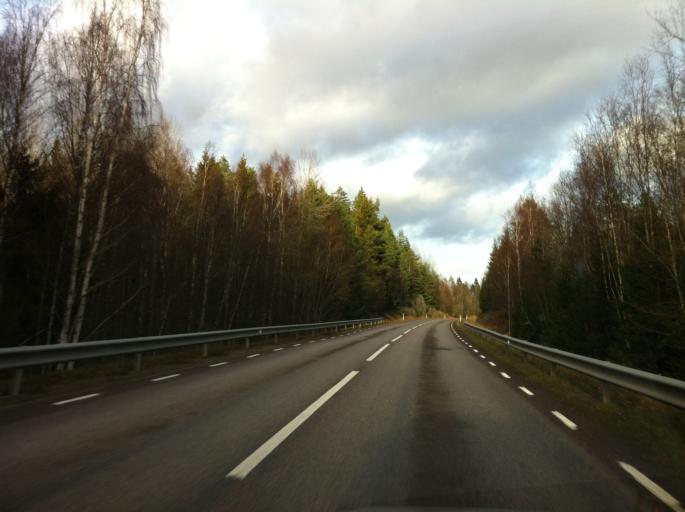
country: SE
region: Kronoberg
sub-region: Uppvidinge Kommun
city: Aseda
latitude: 57.1721
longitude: 15.4948
